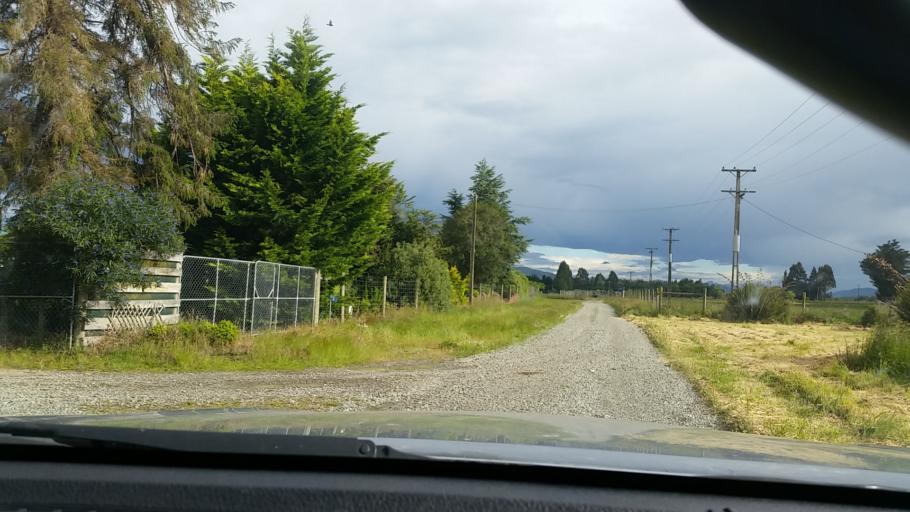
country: NZ
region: Southland
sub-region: Southland District
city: Winton
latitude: -45.8900
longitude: 168.3576
